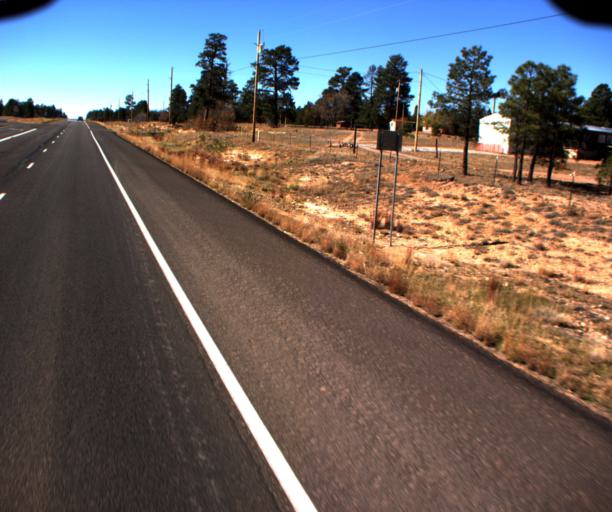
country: US
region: Arizona
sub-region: Apache County
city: Saint Michaels
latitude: 35.6753
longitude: -109.1867
